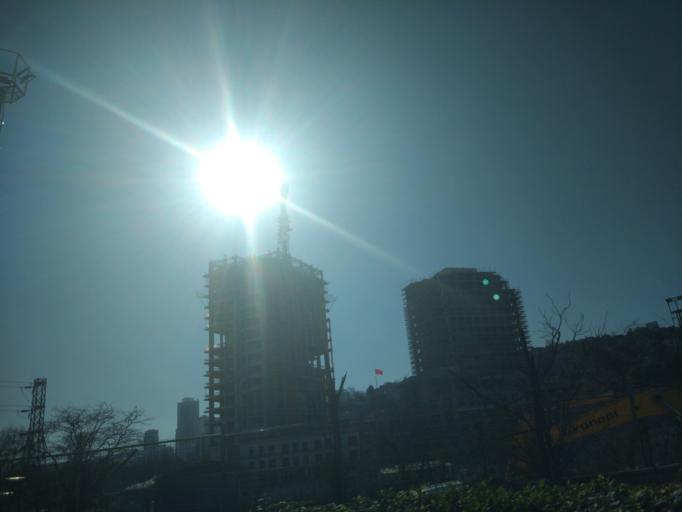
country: TR
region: Istanbul
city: Esenyurt
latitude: 41.0617
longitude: 28.7005
